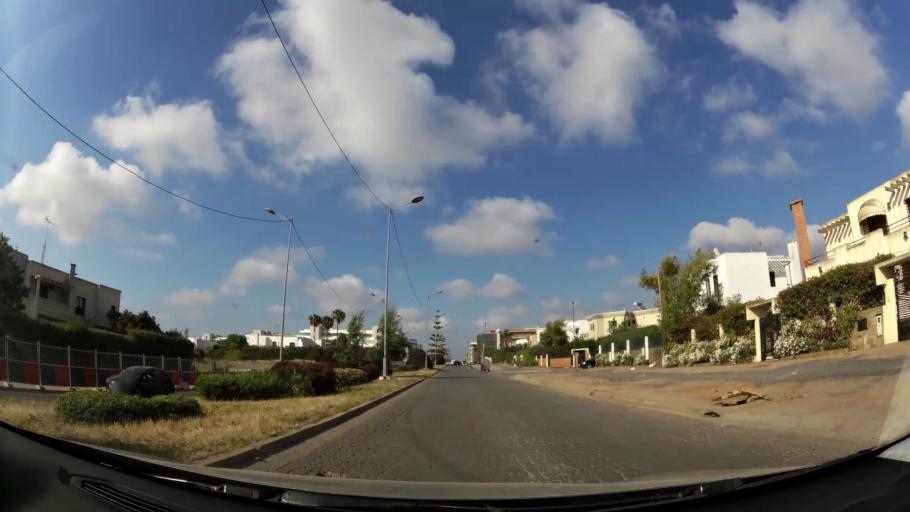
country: MA
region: Rabat-Sale-Zemmour-Zaer
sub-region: Skhirate-Temara
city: Temara
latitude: 33.9515
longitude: -6.8664
